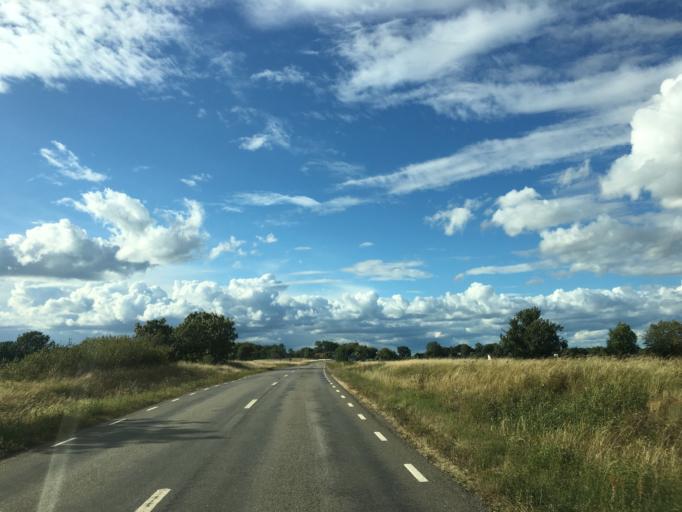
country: SE
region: Kalmar
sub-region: Morbylanga Kommun
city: Moerbylanga
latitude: 56.4400
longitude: 16.4299
